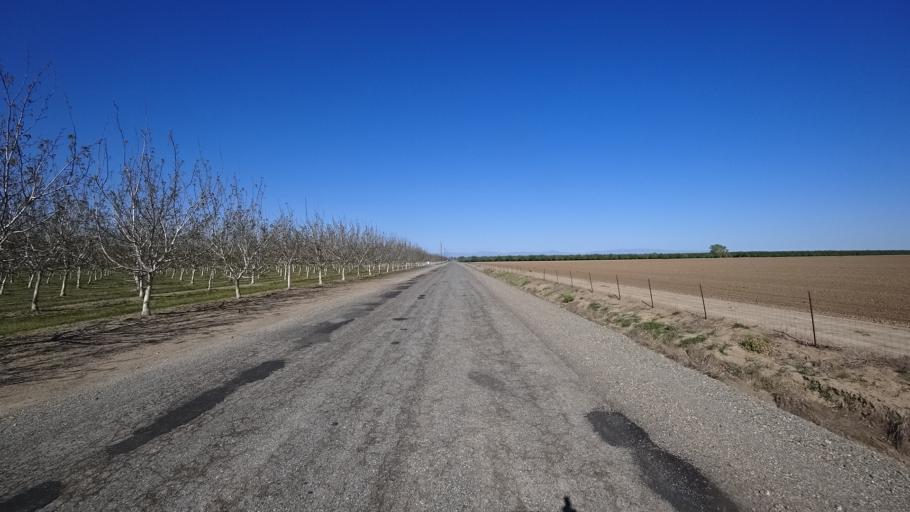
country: US
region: California
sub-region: Glenn County
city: Hamilton City
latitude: 39.6783
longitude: -122.0486
